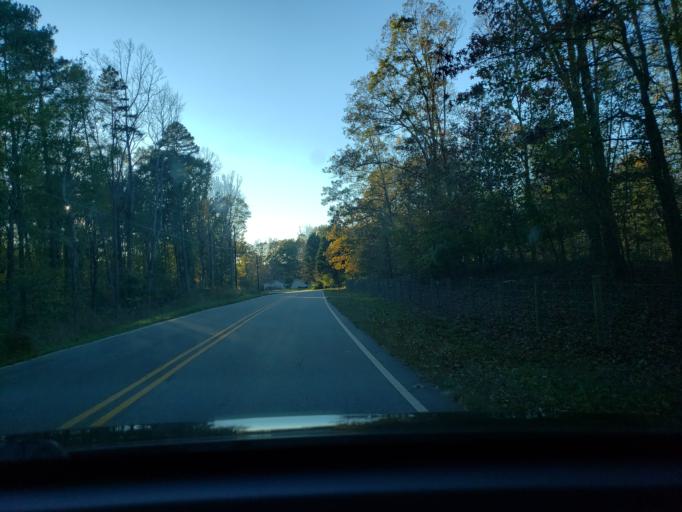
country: US
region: North Carolina
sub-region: Forsyth County
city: Walkertown
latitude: 36.2220
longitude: -80.1747
